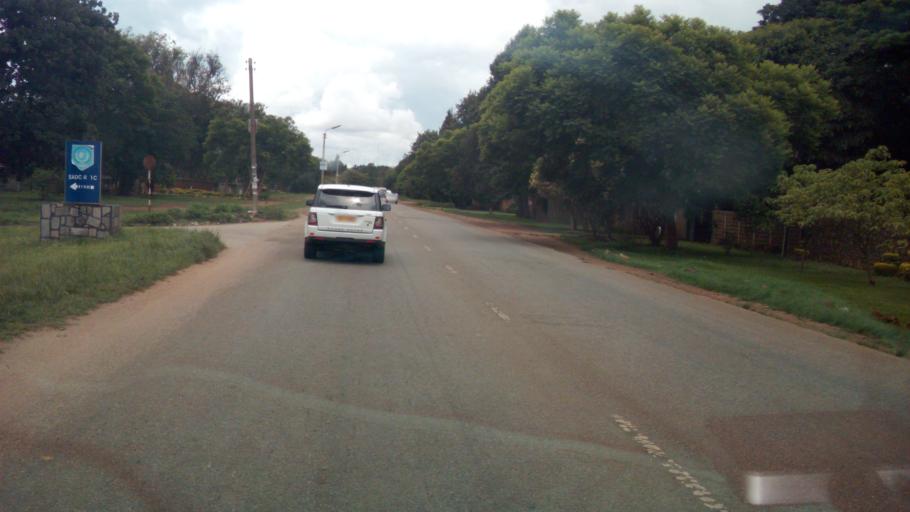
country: ZW
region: Harare
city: Harare
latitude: -17.7517
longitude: 31.0249
